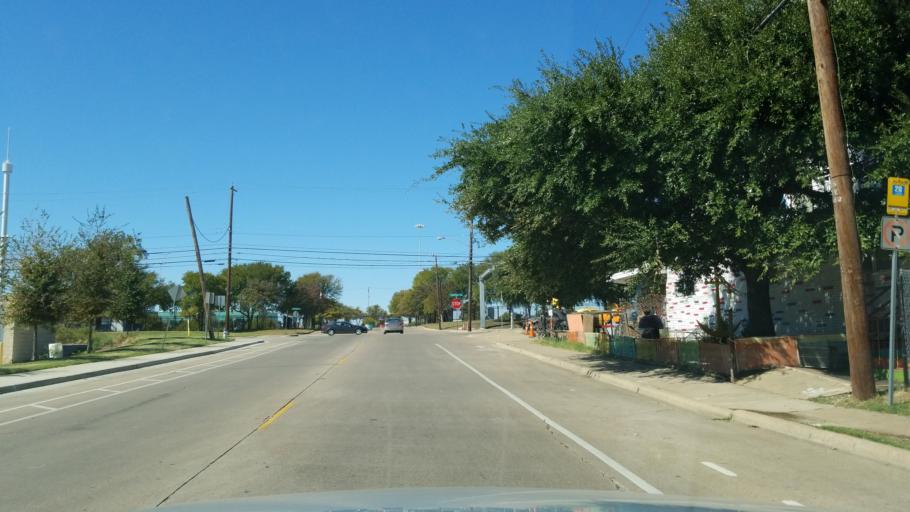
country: US
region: Texas
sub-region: Dallas County
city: Dallas
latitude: 32.7762
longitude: -96.7516
